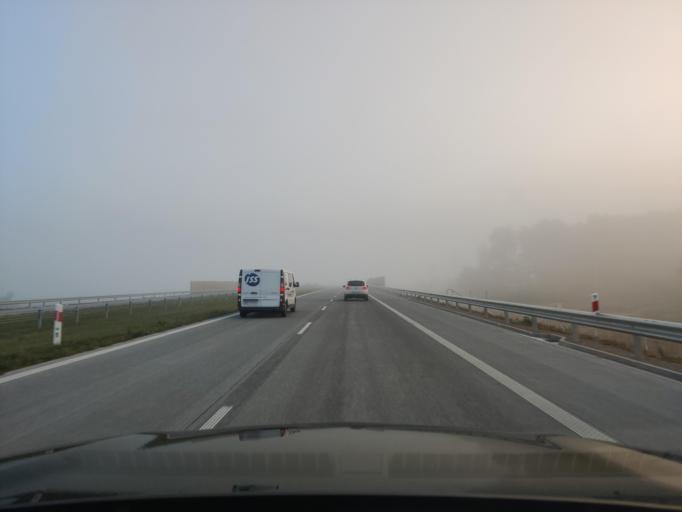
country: PL
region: Masovian Voivodeship
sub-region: Powiat mlawski
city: Strzegowo
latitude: 52.9675
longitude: 20.3175
